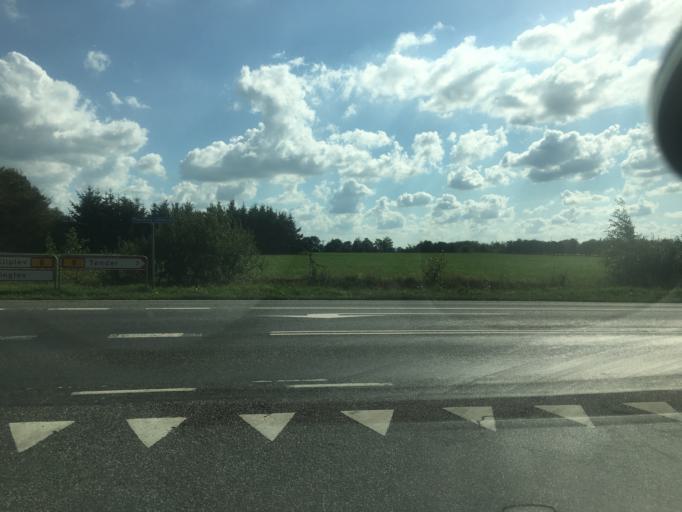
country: DE
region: Schleswig-Holstein
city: Ellhoft
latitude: 54.9350
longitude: 8.9693
